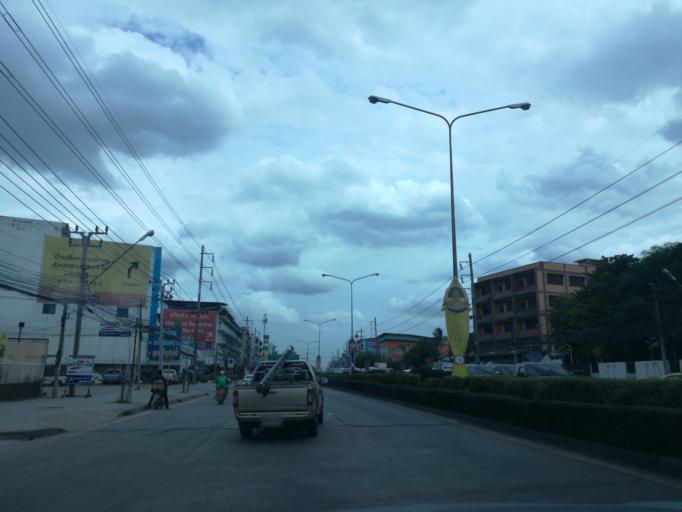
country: TH
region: Bangkok
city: Bang Khun Thian
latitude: 13.6614
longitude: 100.4294
